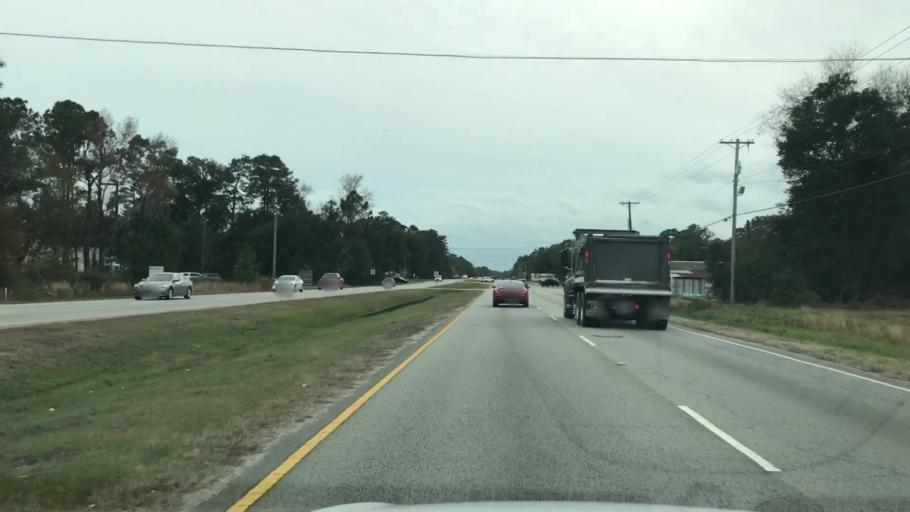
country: US
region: South Carolina
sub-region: Georgetown County
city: Murrells Inlet
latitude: 33.5473
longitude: -79.0500
